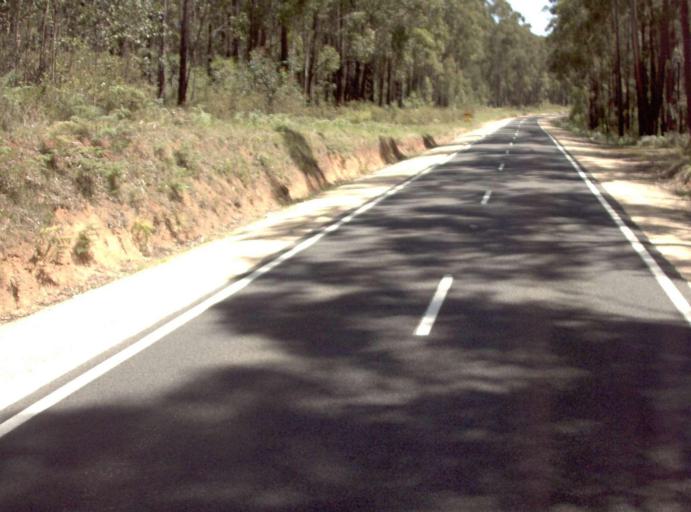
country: AU
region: New South Wales
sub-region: Bombala
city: Bombala
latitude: -37.5737
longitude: 149.0235
